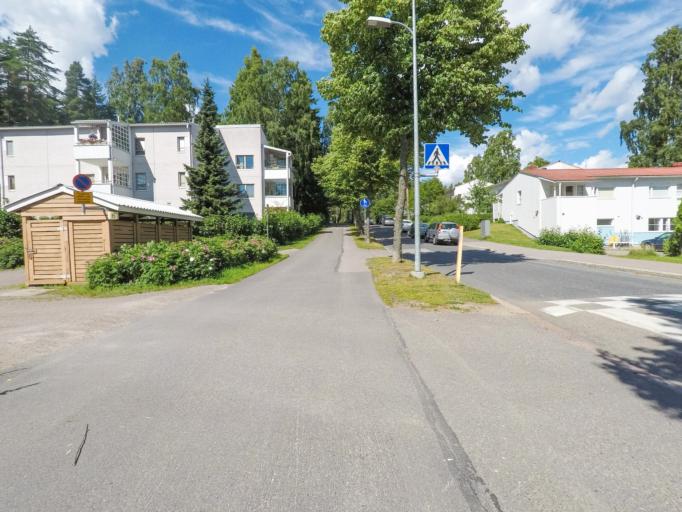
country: FI
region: Uusimaa
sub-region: Helsinki
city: Vantaa
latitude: 60.2198
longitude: 25.0913
